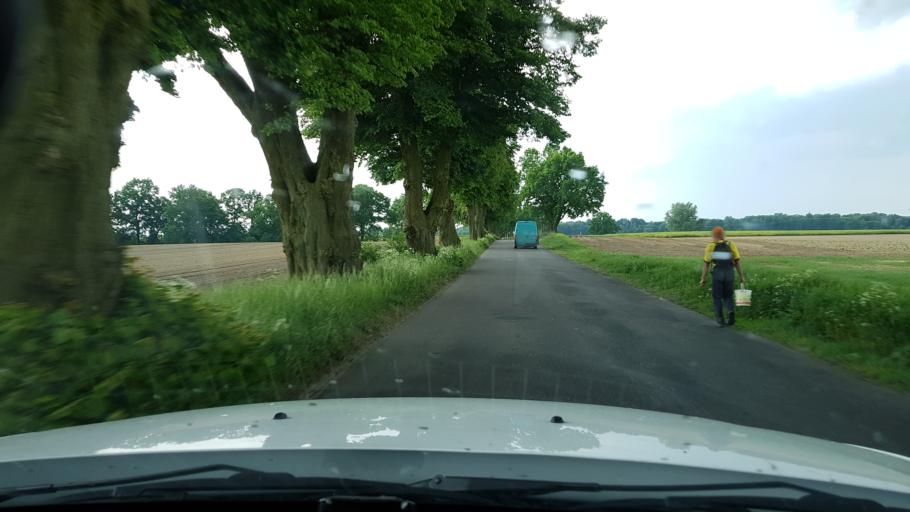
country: PL
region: West Pomeranian Voivodeship
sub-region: Powiat stargardzki
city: Marianowo
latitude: 53.3099
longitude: 15.1773
